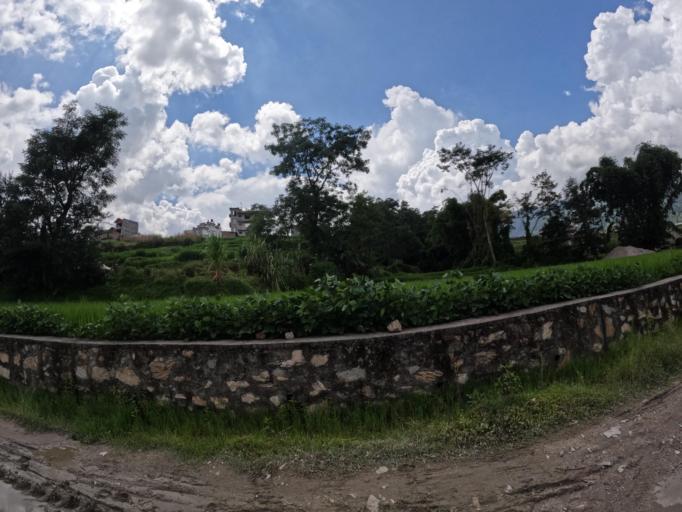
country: NP
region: Central Region
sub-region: Bagmati Zone
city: Kathmandu
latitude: 27.7785
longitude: 85.3284
